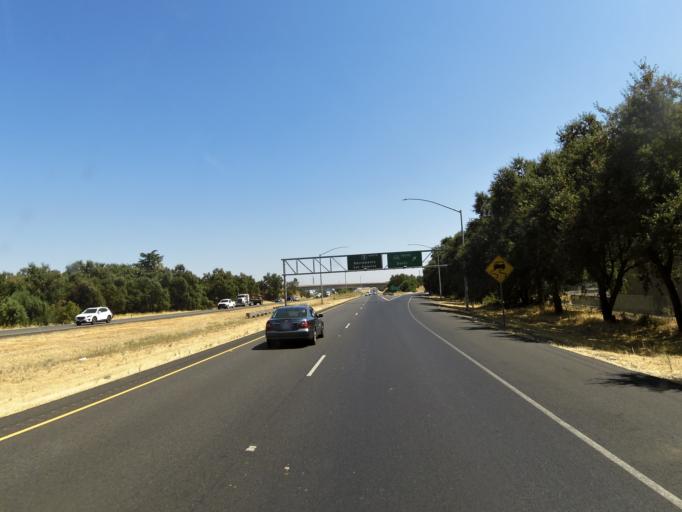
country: US
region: California
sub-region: Yolo County
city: Woodland
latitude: 38.6868
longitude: -121.7529
